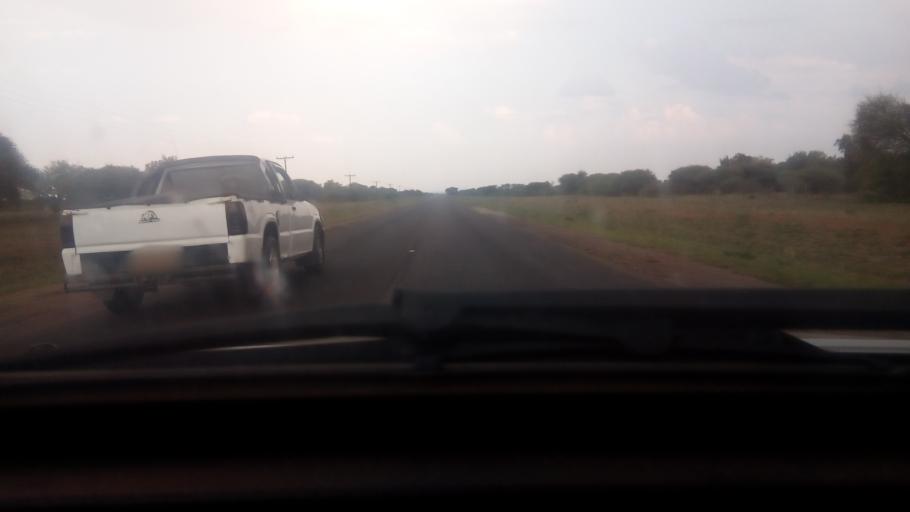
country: BW
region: Kweneng
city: Metsemotlhaba
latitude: -24.4831
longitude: 25.7338
